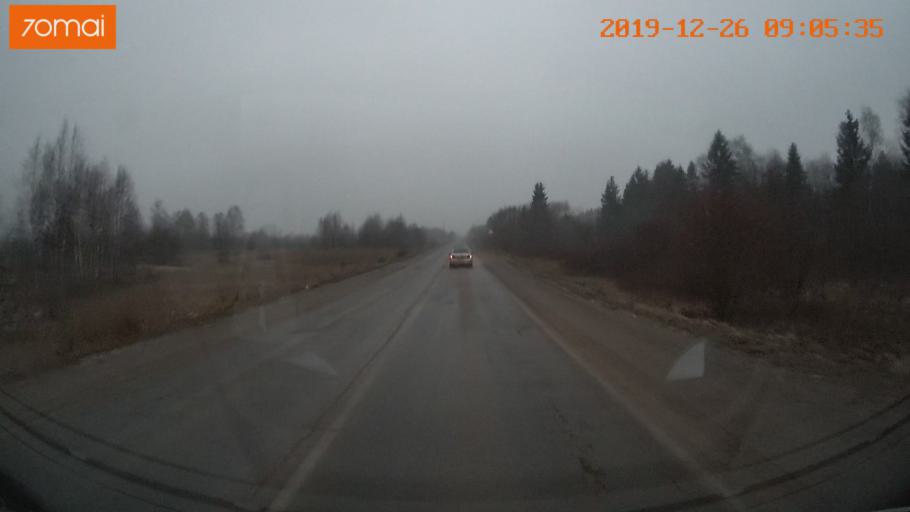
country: RU
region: Vologda
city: Gryazovets
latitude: 58.8270
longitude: 40.2573
